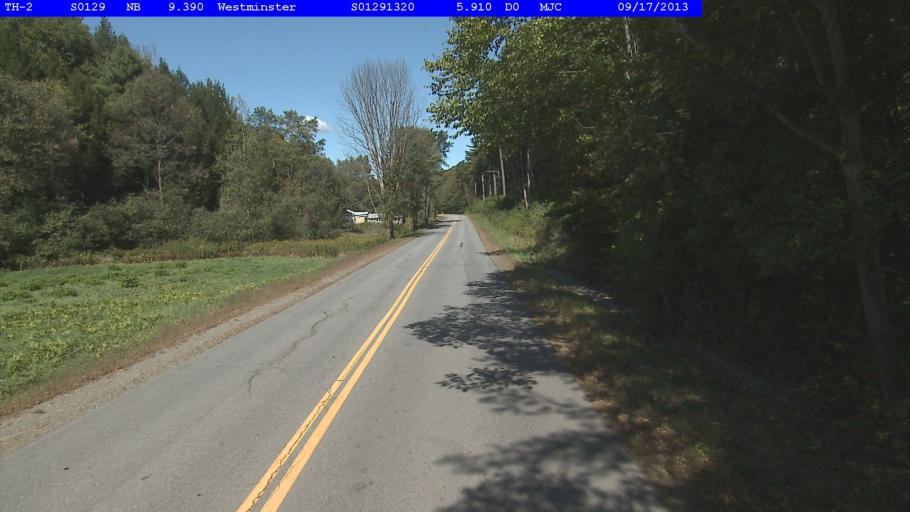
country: US
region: Vermont
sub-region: Windham County
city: Bellows Falls
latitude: 43.0999
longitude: -72.5364
